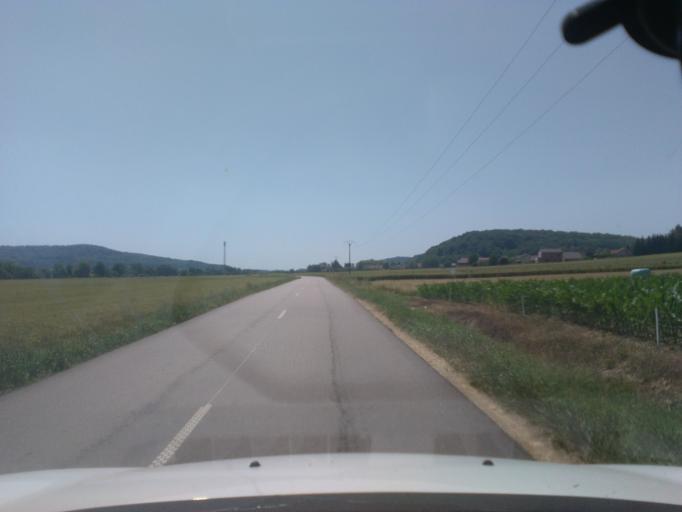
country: FR
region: Lorraine
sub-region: Departement des Vosges
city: Liffol-le-Grand
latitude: 48.3725
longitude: 5.6131
